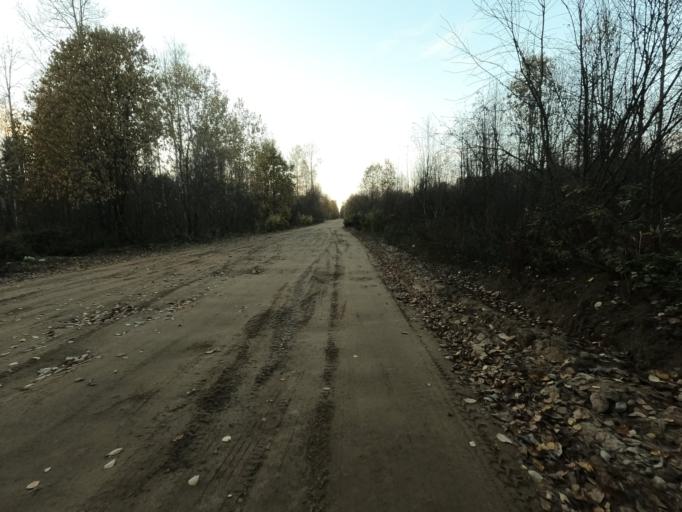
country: RU
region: Leningrad
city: Mga
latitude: 59.7557
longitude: 31.2777
